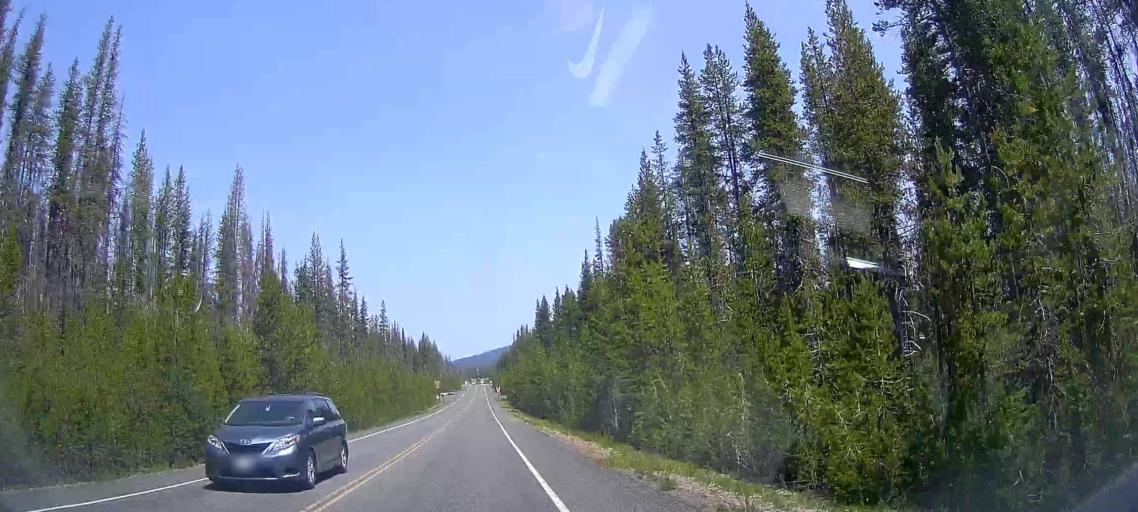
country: US
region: Oregon
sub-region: Lane County
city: Oakridge
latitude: 43.0743
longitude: -122.1185
